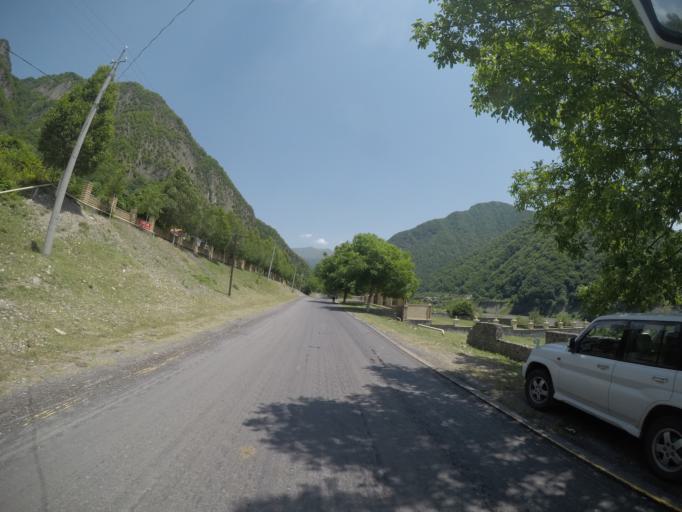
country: AZ
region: Qakh Rayon
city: Qaxbas
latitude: 41.4544
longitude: 47.0145
